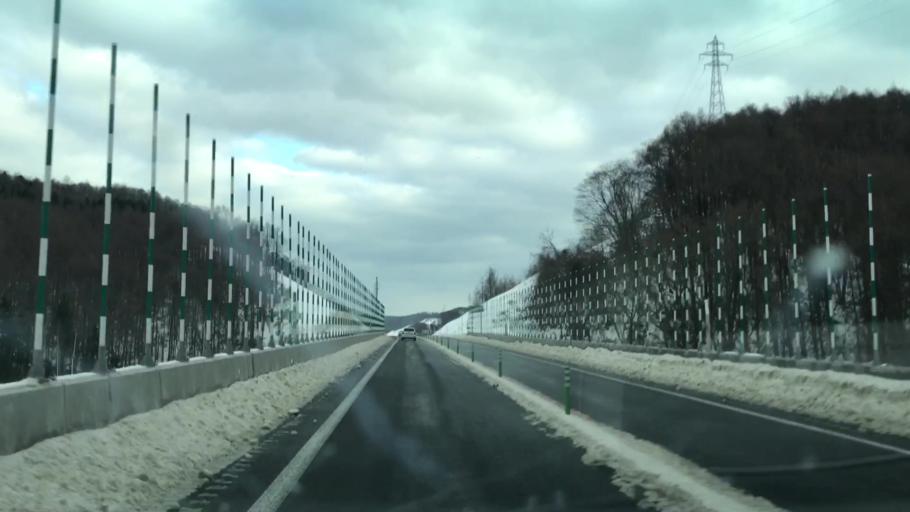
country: JP
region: Hokkaido
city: Otaru
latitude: 43.1966
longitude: 140.9074
